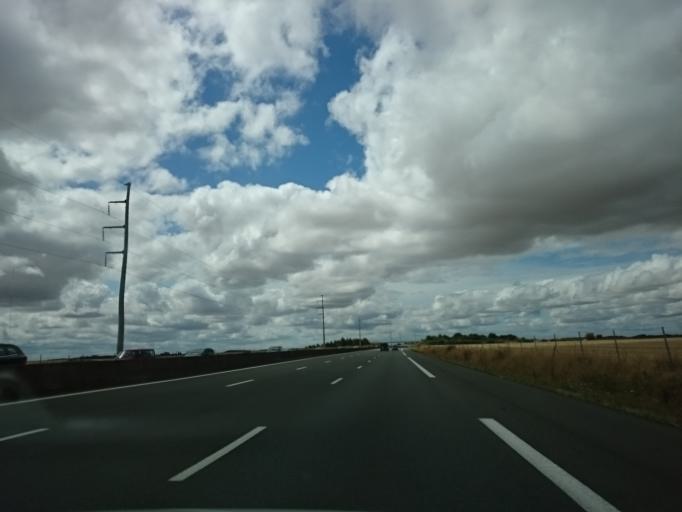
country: FR
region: Centre
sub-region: Departement d'Eure-et-Loir
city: Bailleau-le-Pin
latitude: 48.3324
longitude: 1.3894
